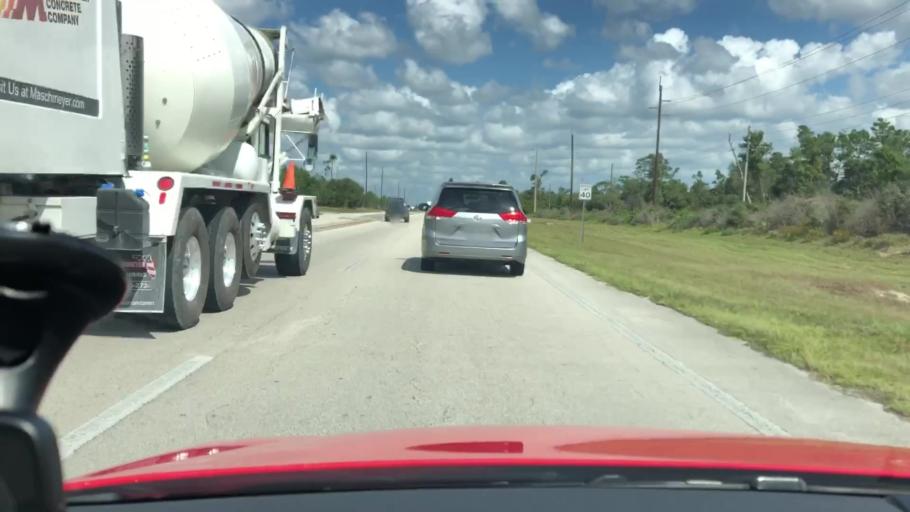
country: US
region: Florida
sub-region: Volusia County
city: Deltona
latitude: 28.9170
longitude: -81.2818
